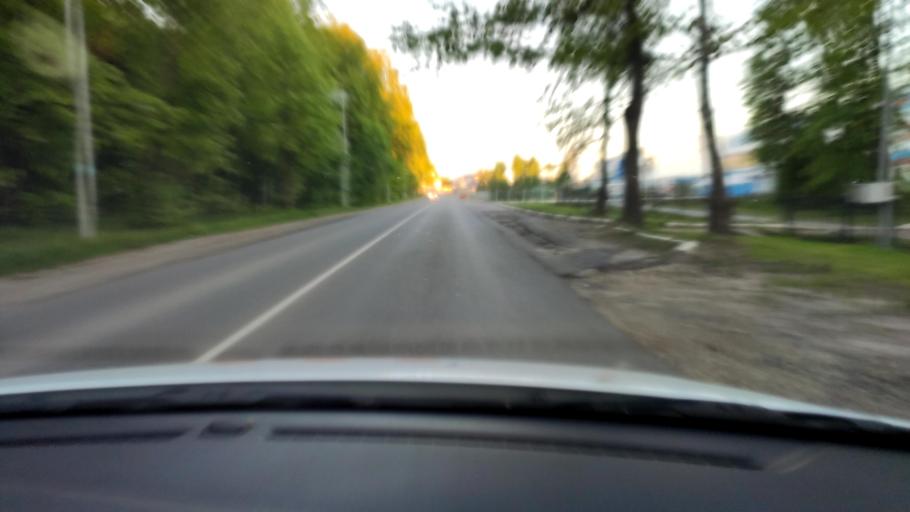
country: RU
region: Tatarstan
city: Vysokaya Gora
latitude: 55.9250
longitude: 49.3039
